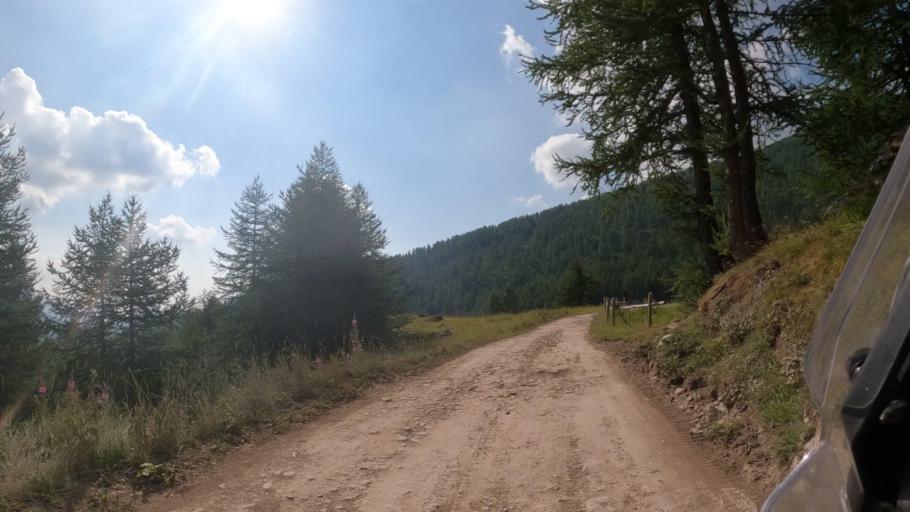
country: IT
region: Piedmont
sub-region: Provincia di Cuneo
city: Briga Alta
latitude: 44.1292
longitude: 7.6800
